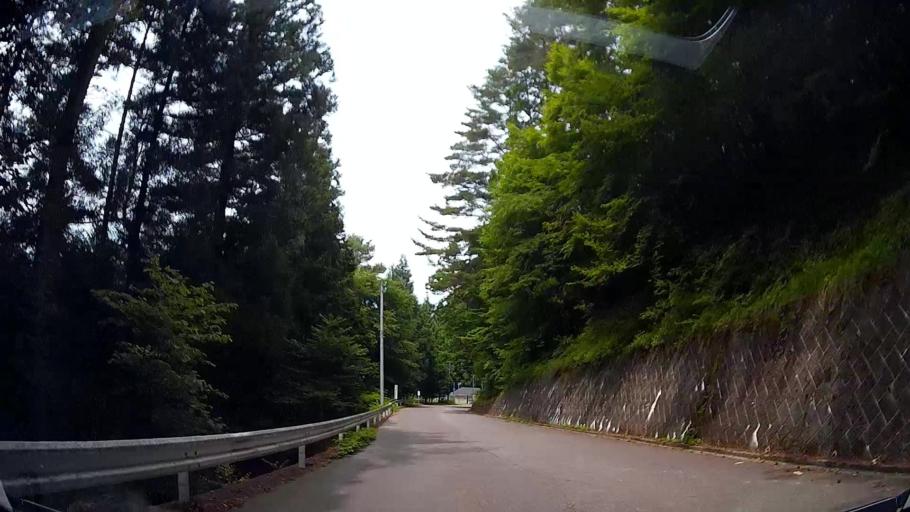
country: JP
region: Nagano
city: Iida
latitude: 35.2893
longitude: 137.9248
